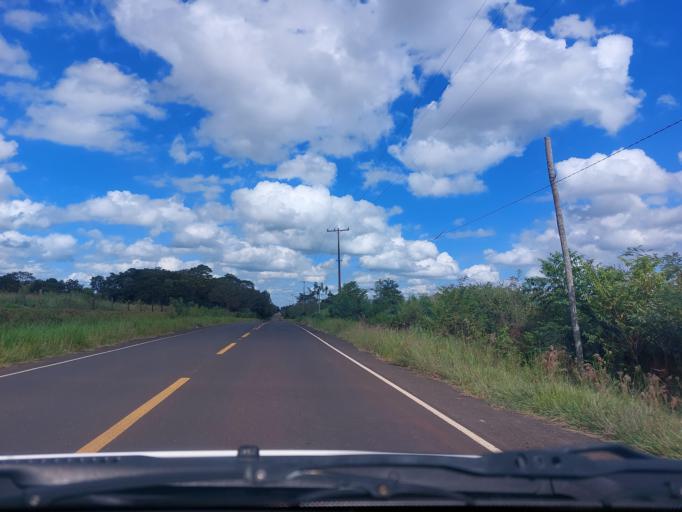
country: PY
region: San Pedro
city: Guayaybi
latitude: -24.5817
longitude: -56.5196
